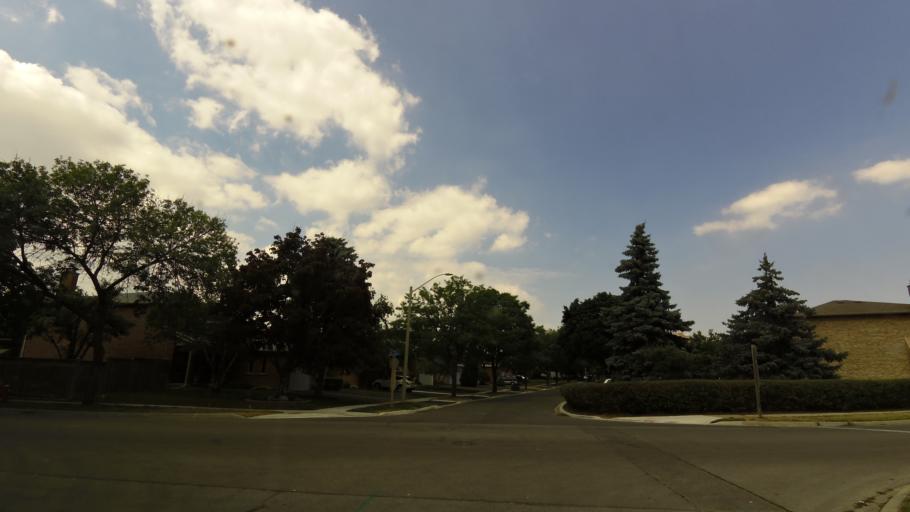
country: CA
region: Ontario
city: Etobicoke
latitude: 43.6193
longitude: -79.6085
